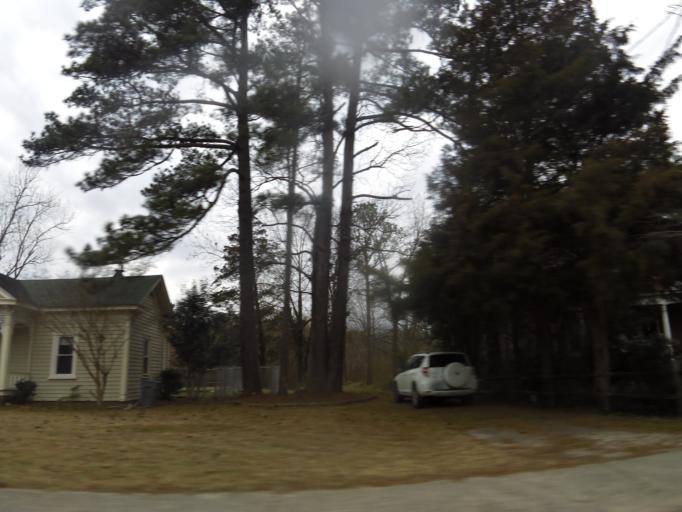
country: US
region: North Carolina
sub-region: Northampton County
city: Jackson
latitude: 36.2720
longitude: -77.2878
